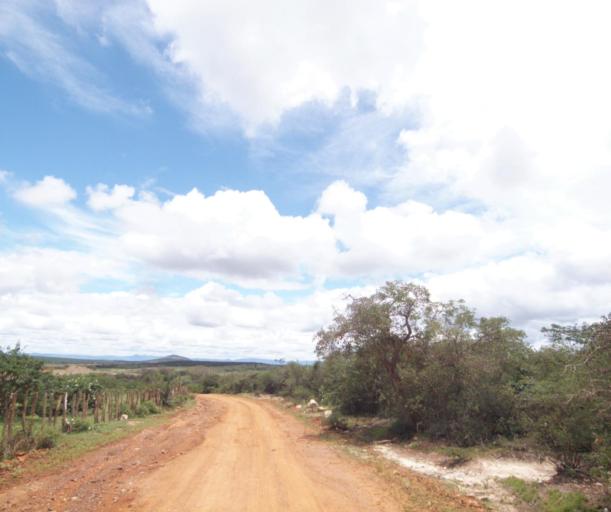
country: BR
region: Bahia
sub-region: Tanhacu
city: Tanhacu
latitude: -14.1876
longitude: -41.0814
